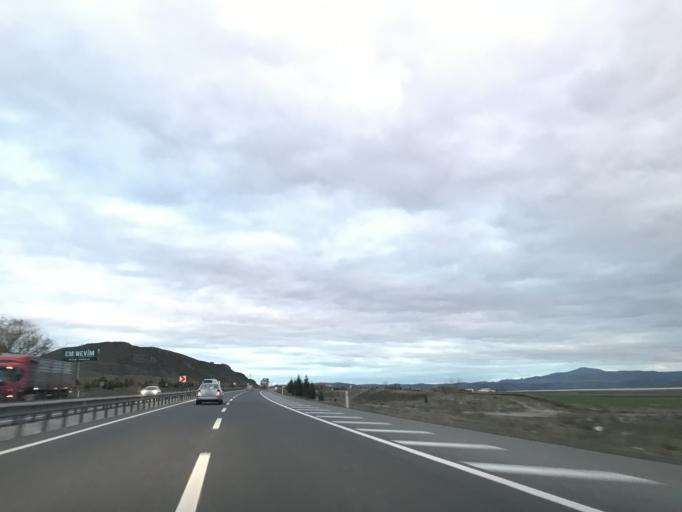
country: TR
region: Ankara
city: Altpinar
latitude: 39.3577
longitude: 32.9136
